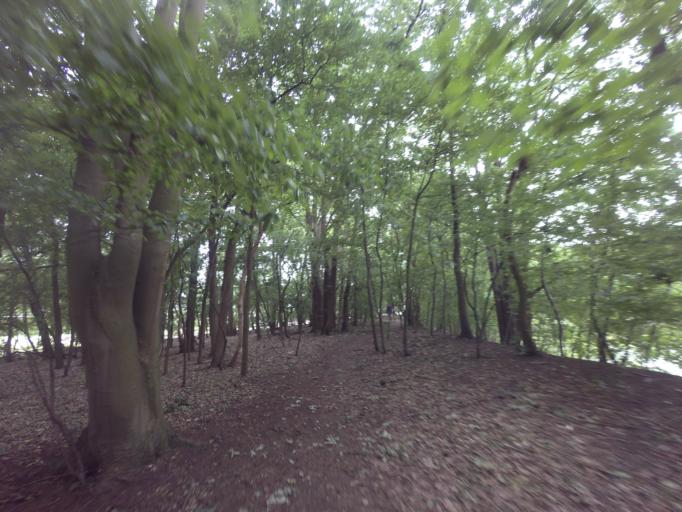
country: BE
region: Flanders
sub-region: Provincie Antwerpen
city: Mechelen
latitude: 51.0600
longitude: 4.4646
